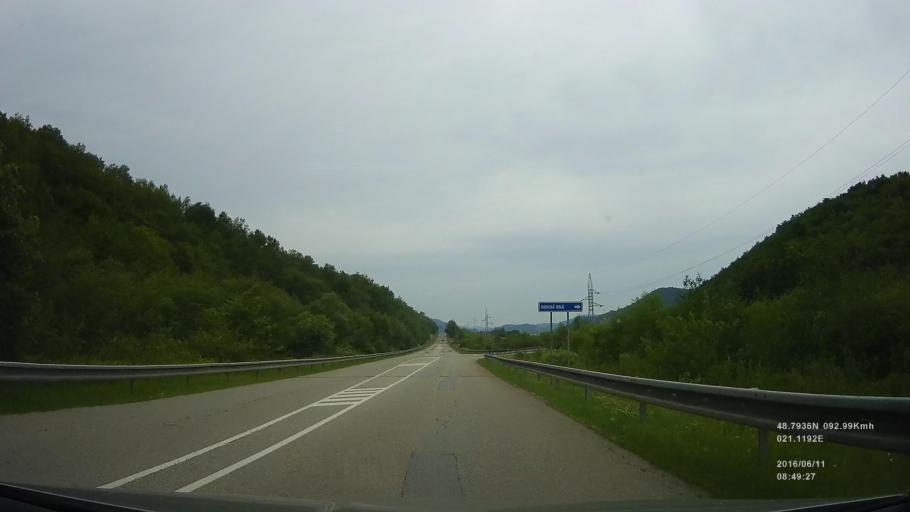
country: SK
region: Kosicky
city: Kosice
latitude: 48.7874
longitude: 21.1252
